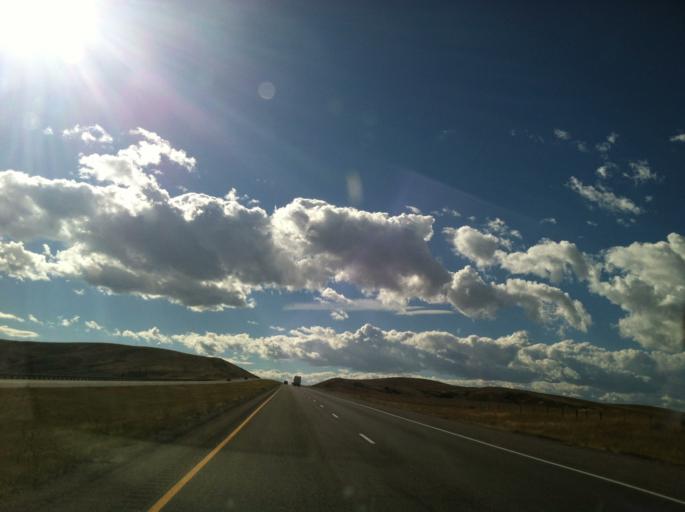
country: US
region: Montana
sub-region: Gallatin County
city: Three Forks
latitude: 45.9201
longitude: -111.6594
